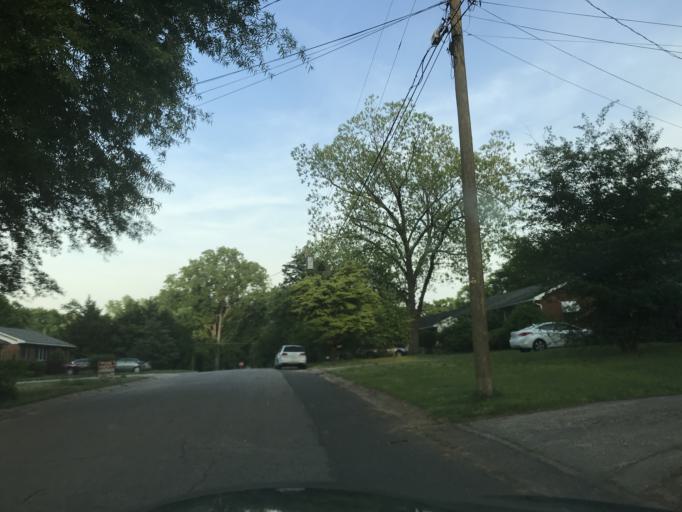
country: US
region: North Carolina
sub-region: Wake County
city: Raleigh
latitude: 35.7914
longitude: -78.6054
